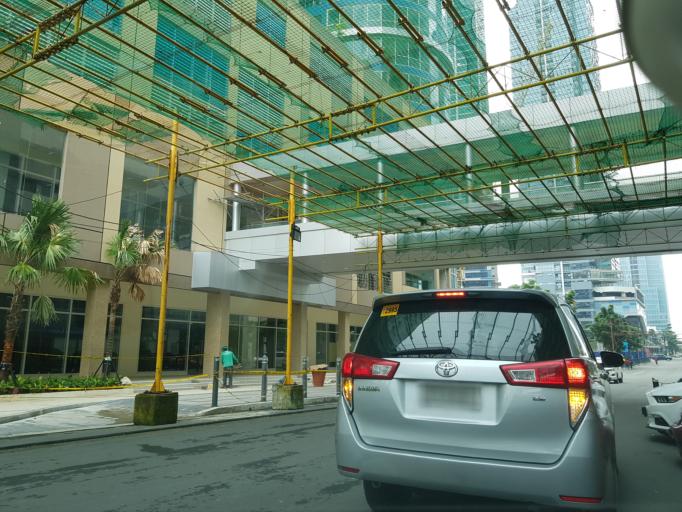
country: PH
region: Metro Manila
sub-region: Makati City
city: Makati City
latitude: 14.5584
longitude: 121.0513
